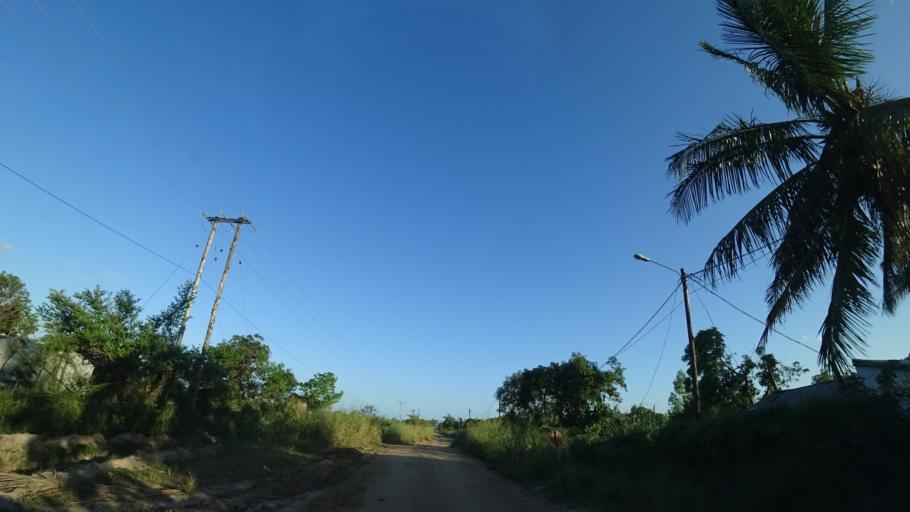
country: MZ
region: Sofala
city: Dondo
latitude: -19.3898
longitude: 34.7084
